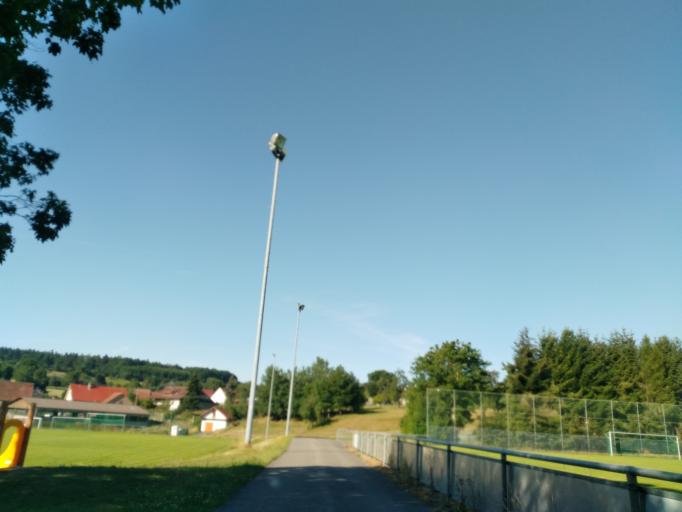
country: DE
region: Baden-Wuerttemberg
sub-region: Karlsruhe Region
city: Limbach
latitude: 49.4818
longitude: 9.2136
